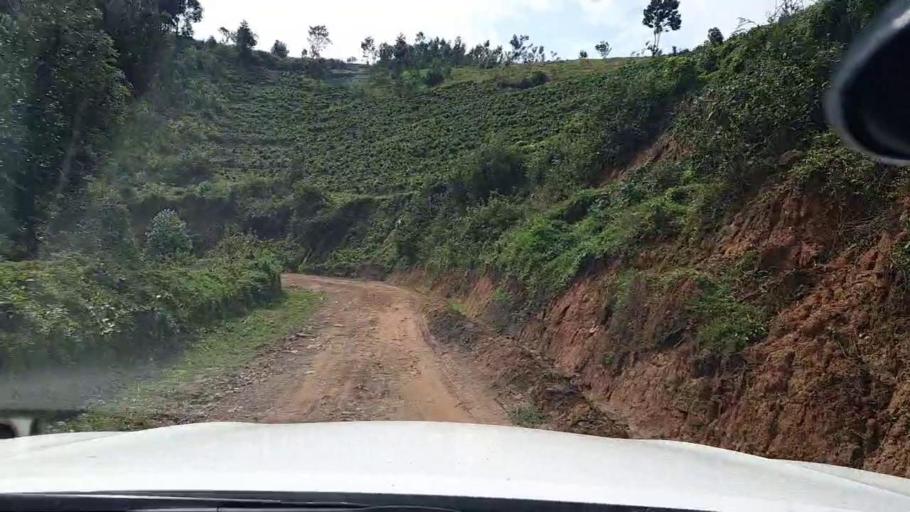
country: RW
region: Western Province
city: Kibuye
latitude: -2.1391
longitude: 29.3764
